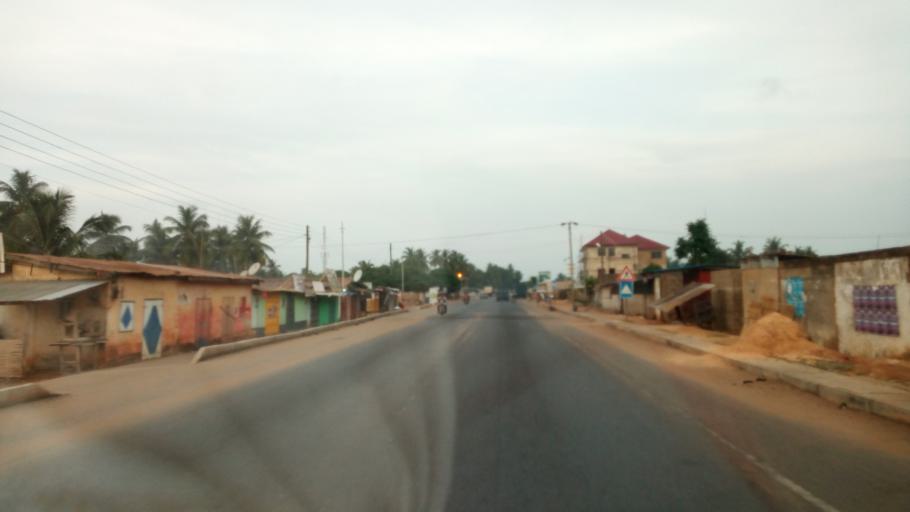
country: TG
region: Maritime
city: Lome
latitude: 6.1154
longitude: 1.1701
